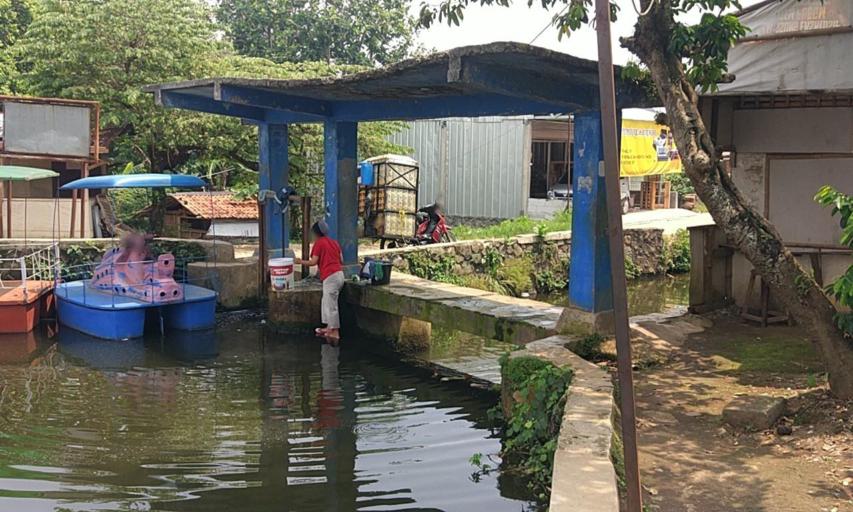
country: ID
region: West Java
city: Ciampea
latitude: -6.5221
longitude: 106.7577
